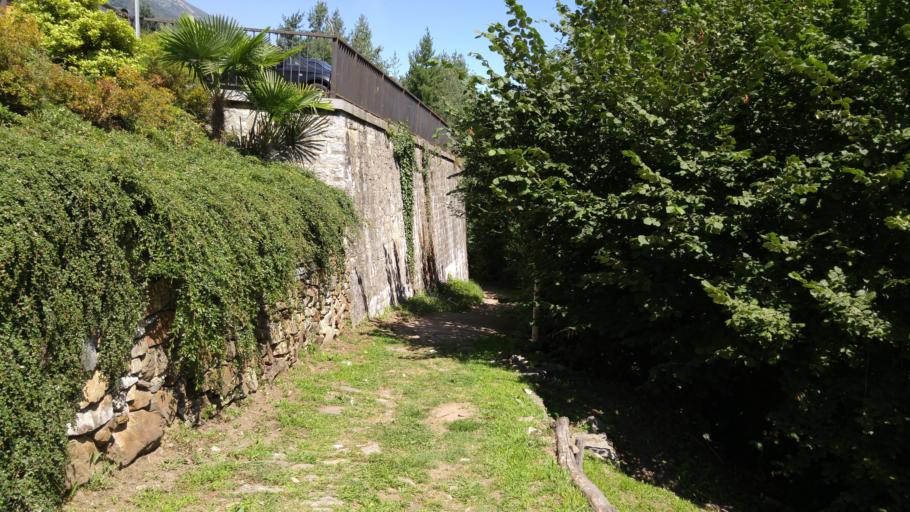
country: IT
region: Piedmont
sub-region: Provincia Verbano-Cusio-Ossola
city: Cannobio
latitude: 46.0722
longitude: 8.6871
